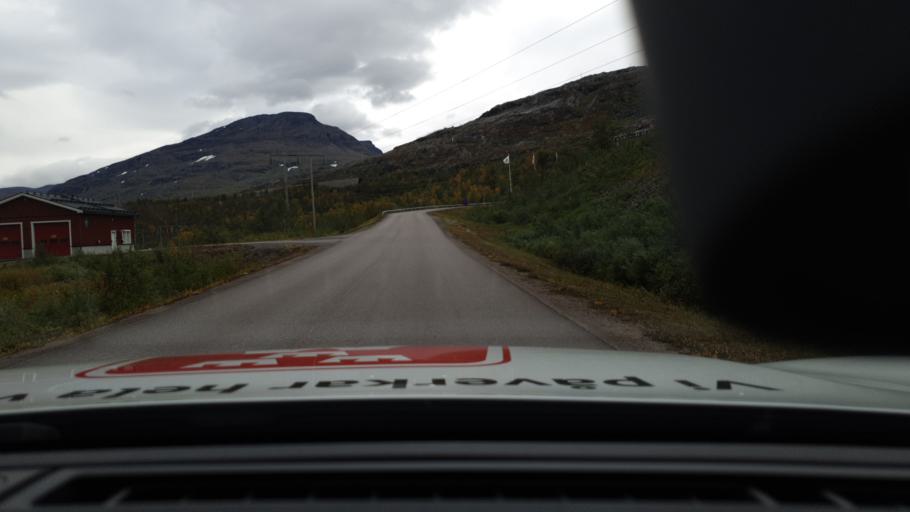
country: NO
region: Troms
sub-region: Lavangen
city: Tennevoll
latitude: 68.4295
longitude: 18.1227
